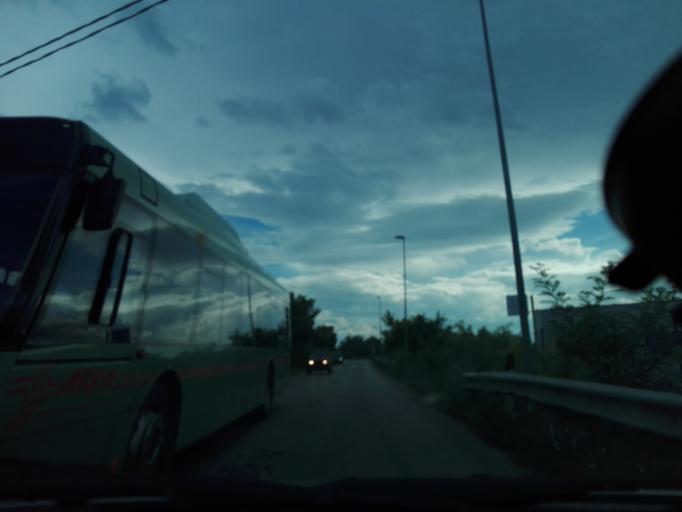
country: IT
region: Abruzzo
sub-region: Provincia di Pescara
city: Cappelle sul Tavo
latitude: 42.4600
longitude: 14.1176
